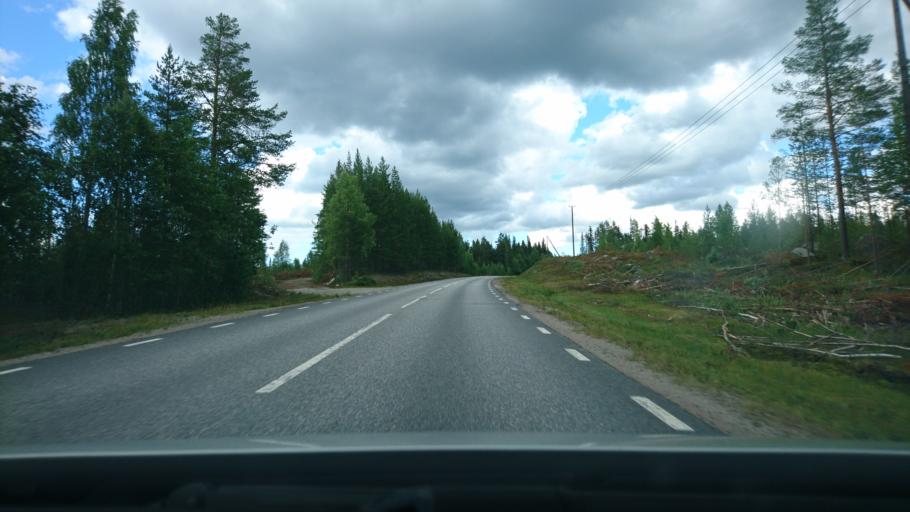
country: SE
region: Vaesterbotten
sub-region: Asele Kommun
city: Asele
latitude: 63.9130
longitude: 17.2267
